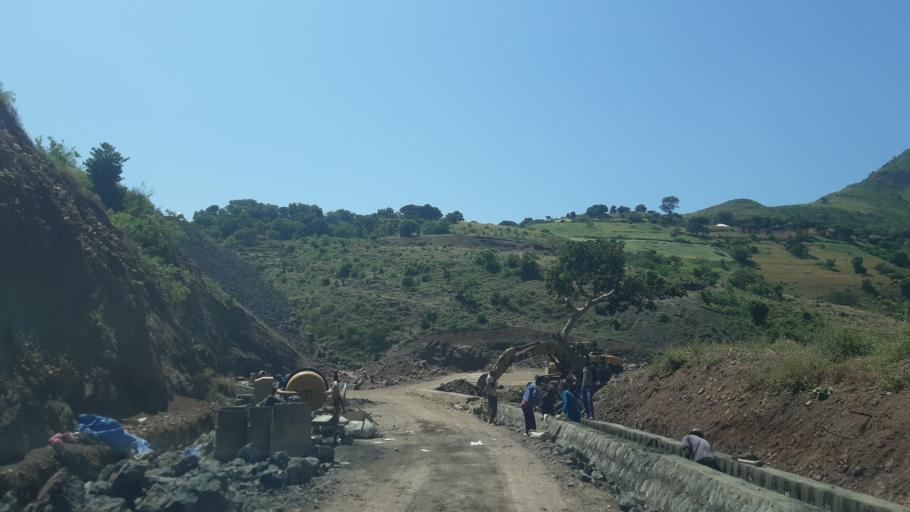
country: ET
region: Amhara
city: Dabat
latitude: 13.1684
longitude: 37.6050
